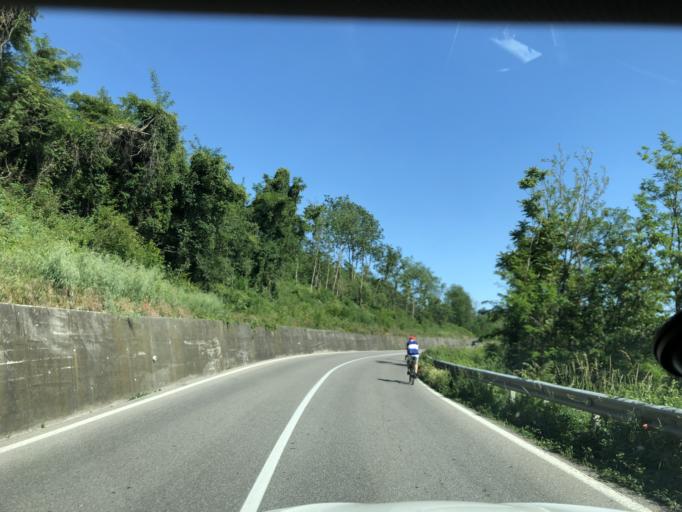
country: IT
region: Lombardy
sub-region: Citta metropolitana di Milano
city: Nosate
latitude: 45.5815
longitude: 8.7084
